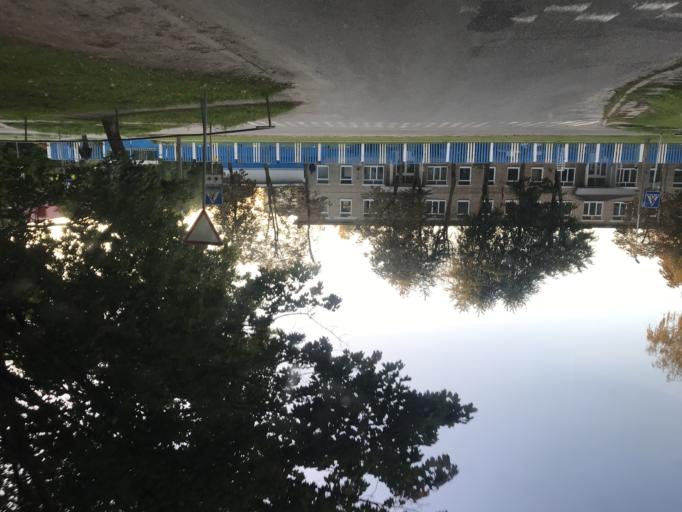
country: BY
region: Mogilev
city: Mahilyow
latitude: 53.9075
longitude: 30.3201
